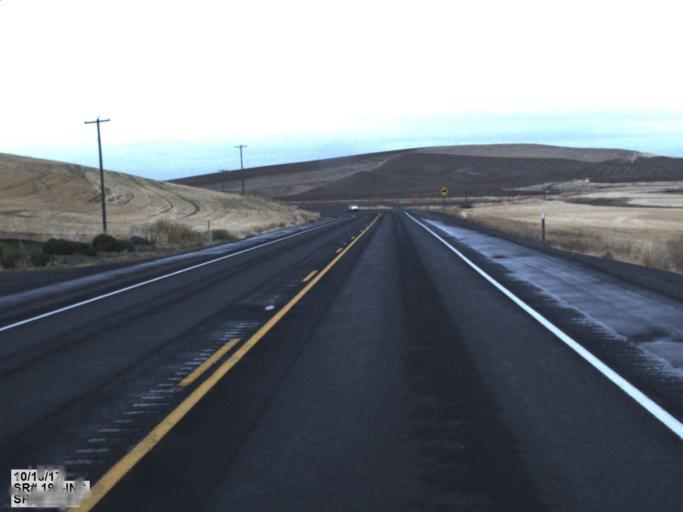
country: US
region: Washington
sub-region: Asotin County
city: Clarkston
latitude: 46.5566
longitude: -117.1040
